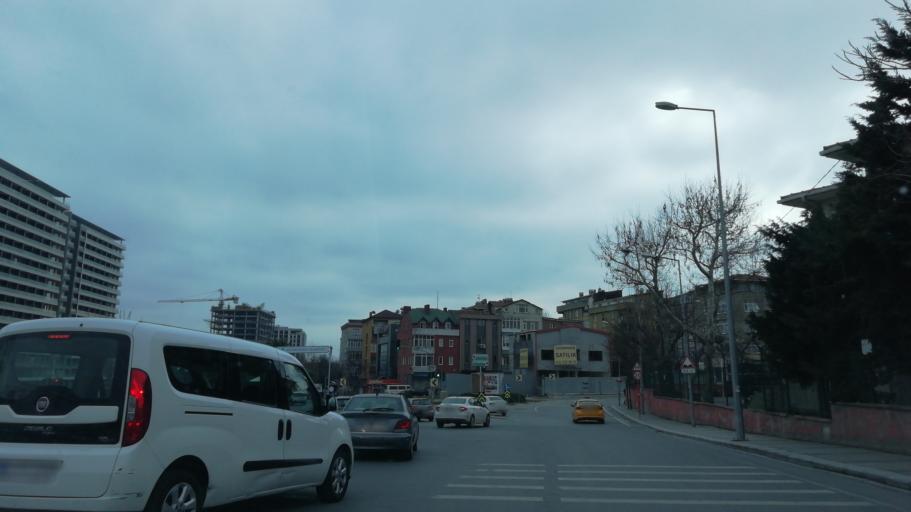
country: TR
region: Istanbul
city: Mahmutbey
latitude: 41.0075
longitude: 28.8077
